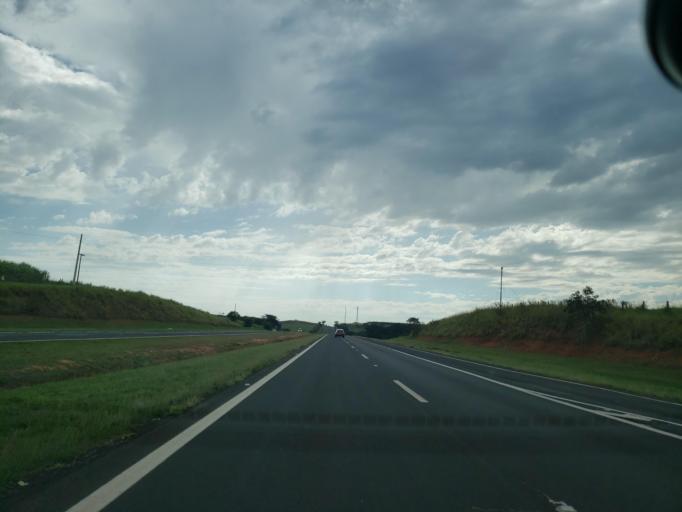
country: BR
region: Sao Paulo
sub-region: Cafelandia
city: Cafelandia
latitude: -21.7731
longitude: -49.6646
